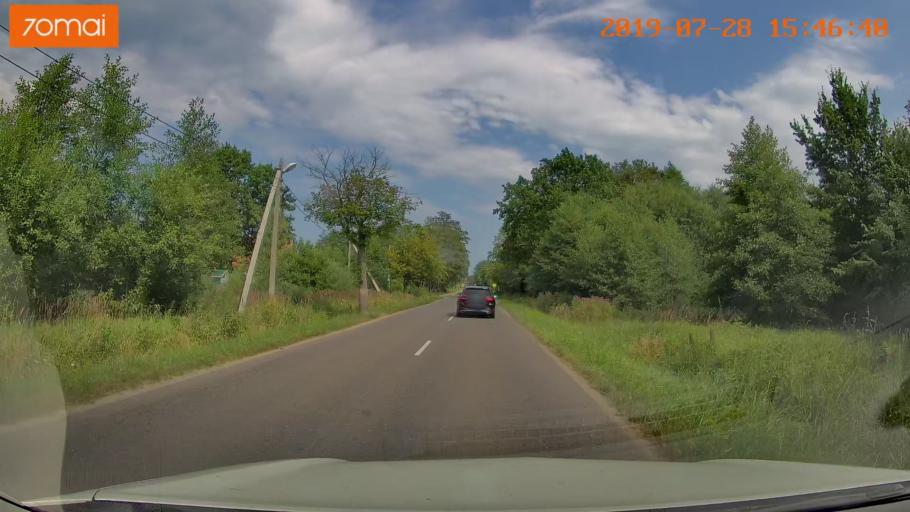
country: RU
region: Kaliningrad
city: Otradnoye
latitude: 54.9428
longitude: 20.0567
